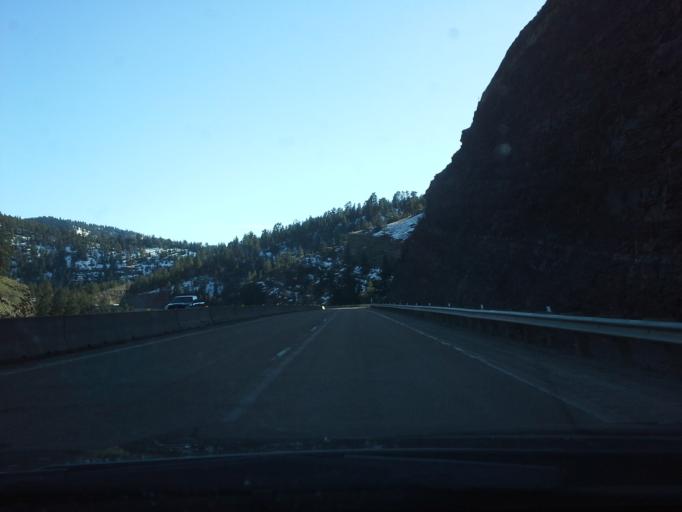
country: US
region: Montana
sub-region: Lewis and Clark County
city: Helena Valley Northwest
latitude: 46.9328
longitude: -112.1267
